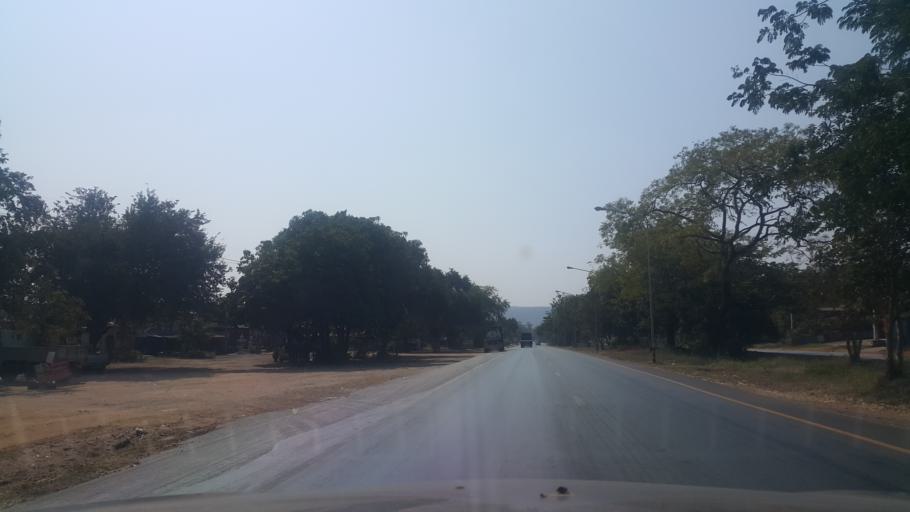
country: TH
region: Nakhon Ratchasima
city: Pak Thong Chai
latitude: 14.6128
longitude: 102.0074
